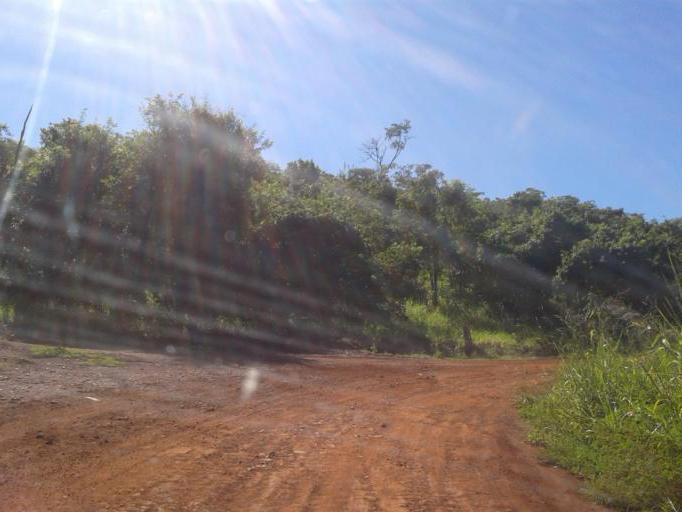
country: BR
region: Minas Gerais
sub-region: Capinopolis
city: Capinopolis
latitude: -18.6808
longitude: -49.6116
